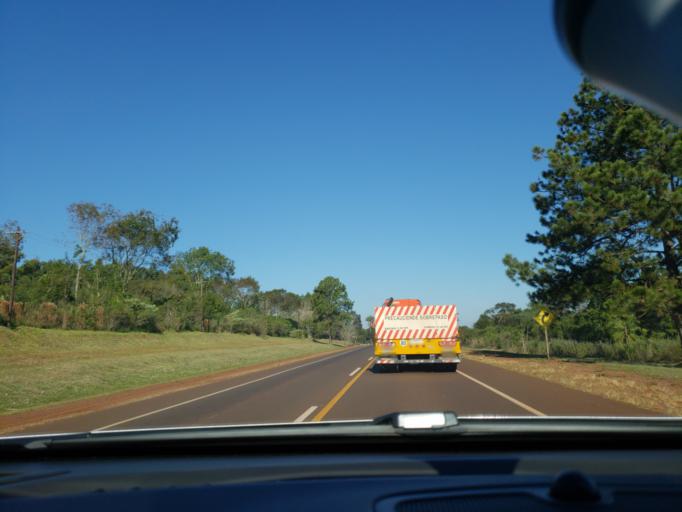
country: AR
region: Misiones
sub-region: Departamento de Apostoles
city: San Jose
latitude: -27.8019
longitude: -55.7688
